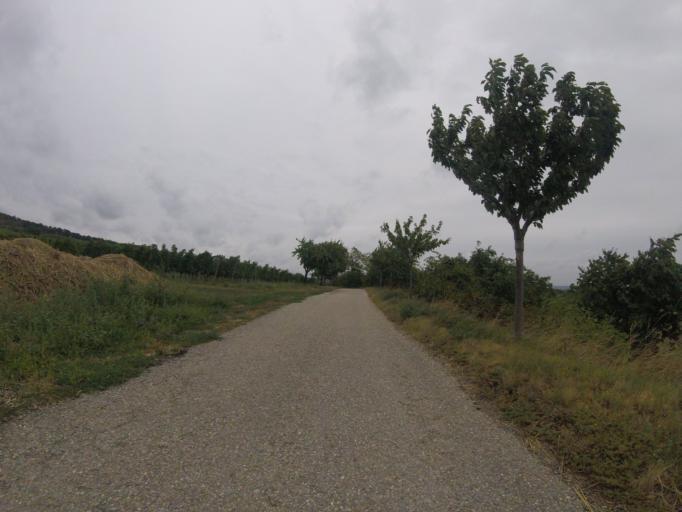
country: AT
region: Burgenland
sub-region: Eisenstadt-Umgebung
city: Breitenbrunn
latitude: 47.9410
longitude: 16.7067
